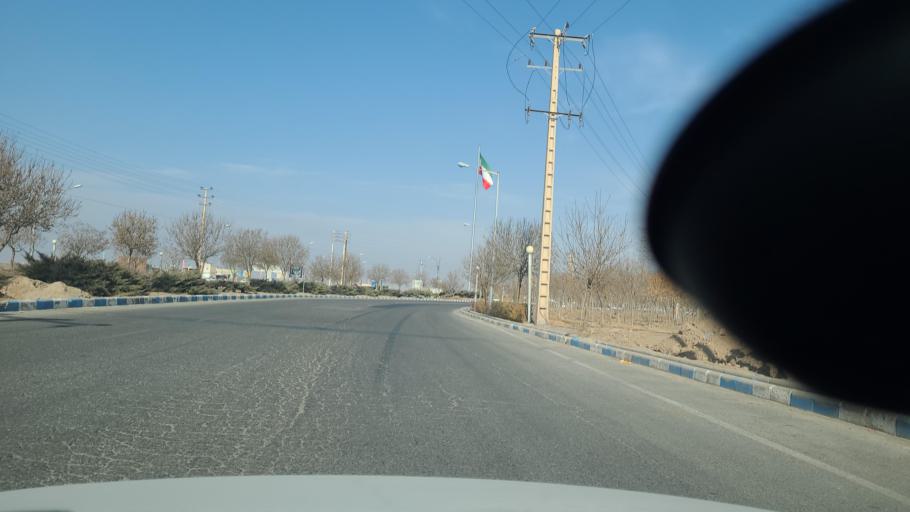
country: IR
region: Razavi Khorasan
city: Fariman
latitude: 35.7045
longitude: 59.8356
